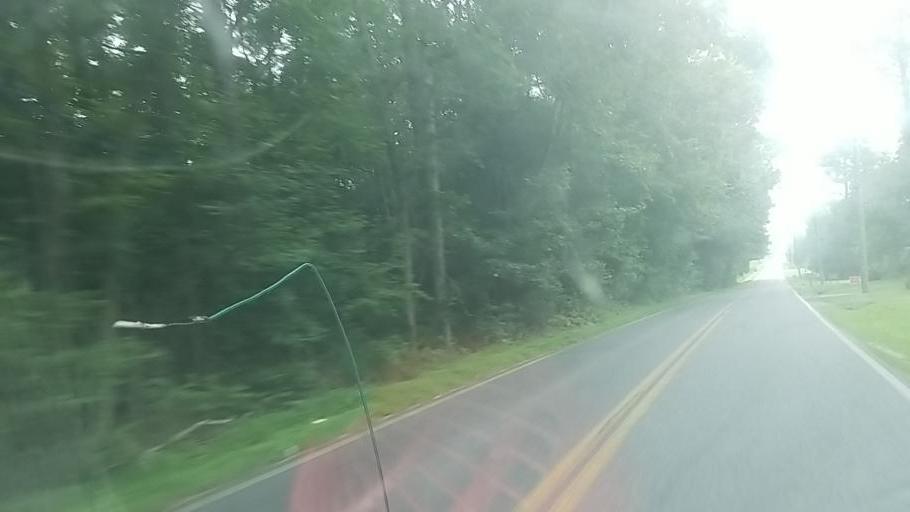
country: US
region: Maryland
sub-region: Wicomico County
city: Salisbury
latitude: 38.3879
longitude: -75.5292
